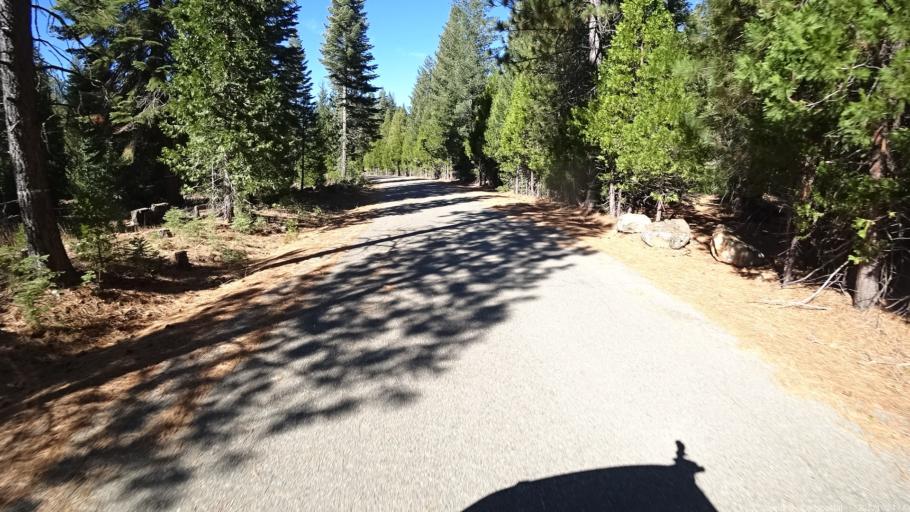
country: US
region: California
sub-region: Shasta County
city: Shingletown
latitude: 40.5133
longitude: -121.6711
